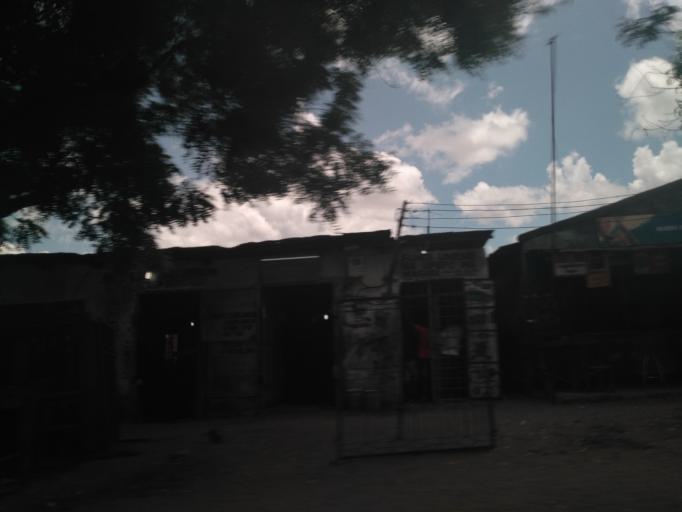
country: TZ
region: Dar es Salaam
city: Dar es Salaam
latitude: -6.8669
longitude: 39.2724
